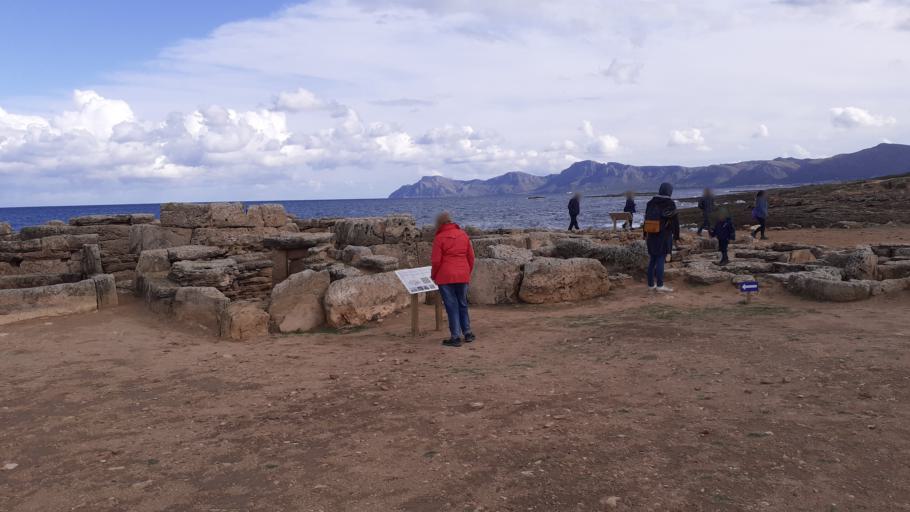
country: ES
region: Balearic Islands
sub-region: Illes Balears
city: Santa Margalida
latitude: 39.7548
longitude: 3.1821
